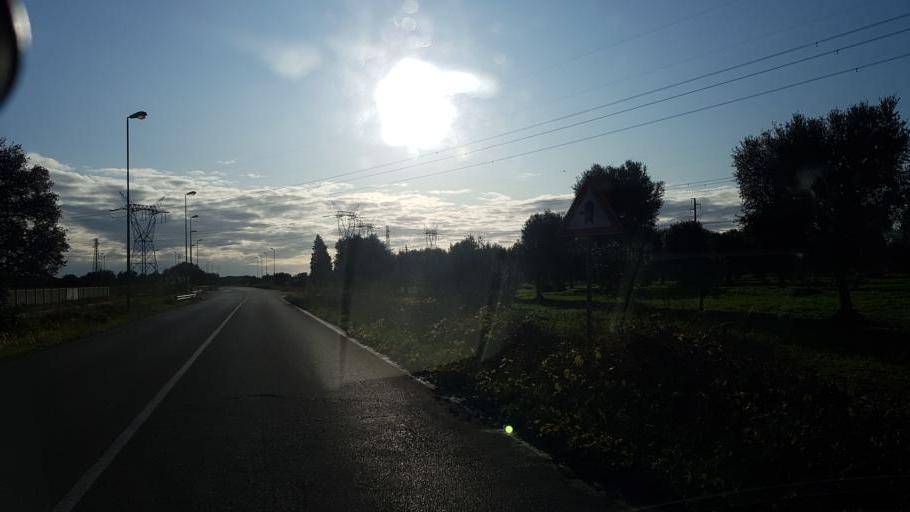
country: IT
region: Apulia
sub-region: Provincia di Brindisi
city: San Pietro Vernotico
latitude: 40.5568
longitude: 18.0267
